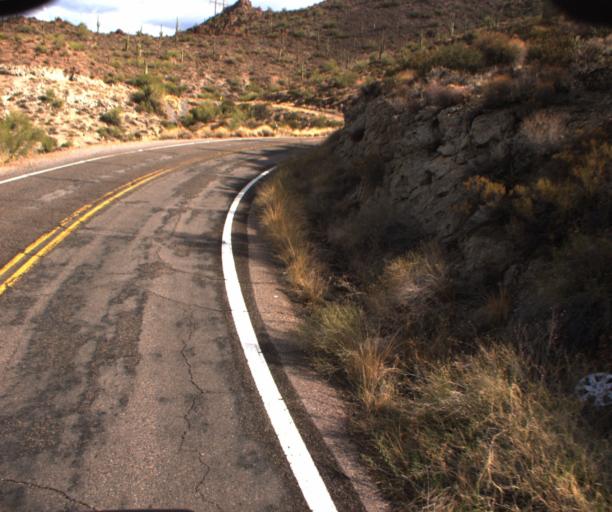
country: US
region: Arizona
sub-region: Pinal County
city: Apache Junction
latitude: 33.5054
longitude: -111.4587
